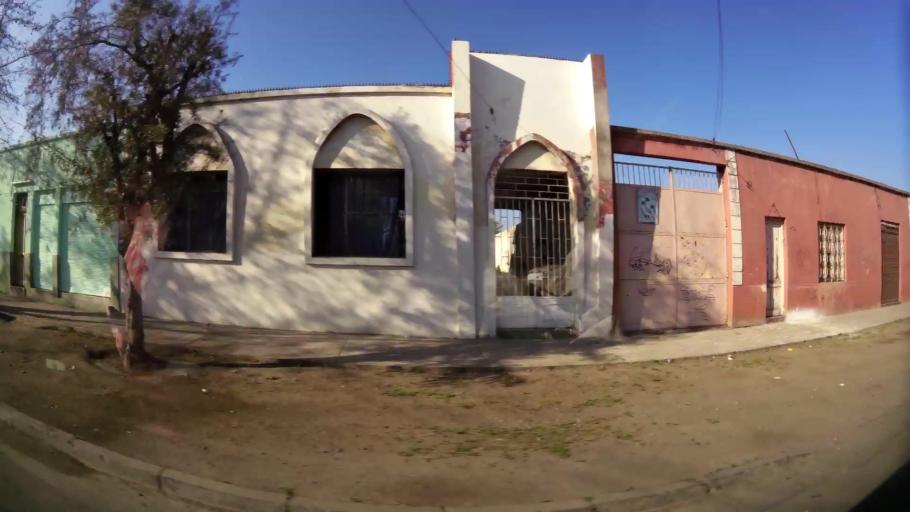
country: CL
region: Santiago Metropolitan
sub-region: Provincia de Santiago
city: Santiago
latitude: -33.4921
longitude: -70.6352
